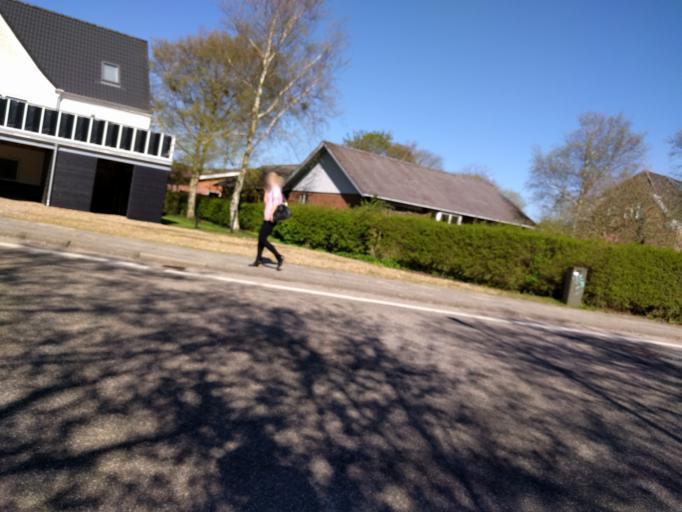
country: DK
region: Central Jutland
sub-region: Ringkobing-Skjern Kommune
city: Ringkobing
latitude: 56.0953
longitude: 8.2509
